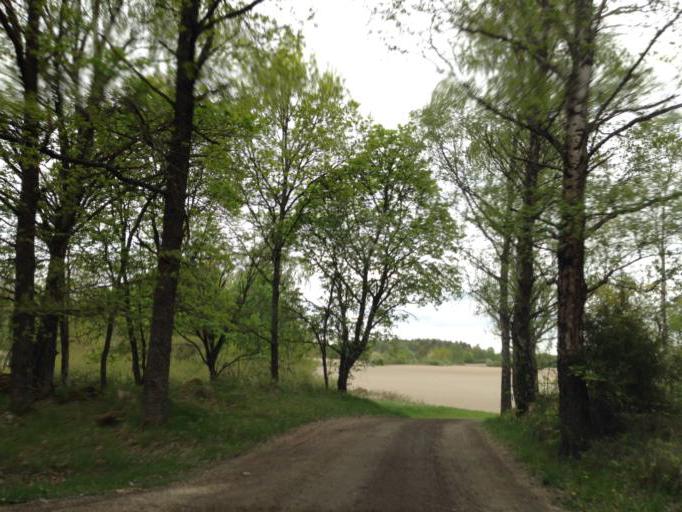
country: SE
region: Soedermanland
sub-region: Eskilstuna Kommun
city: Kvicksund
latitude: 59.4381
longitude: 16.3006
